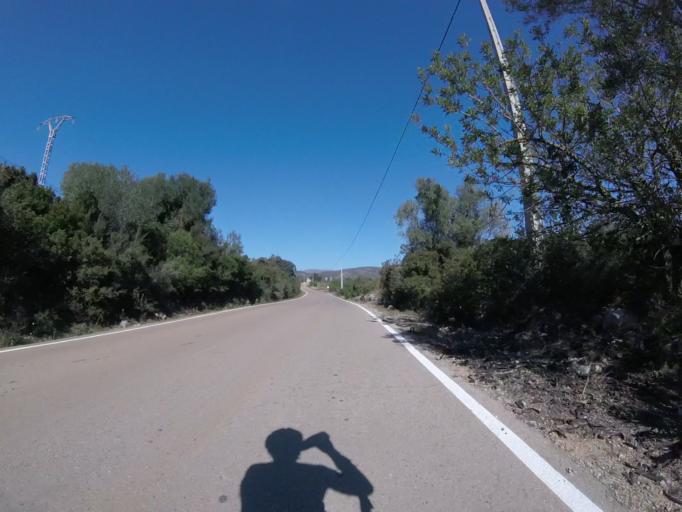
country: ES
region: Valencia
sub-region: Provincia de Castello
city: Santa Magdalena de Pulpis
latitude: 40.3624
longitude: 0.2813
